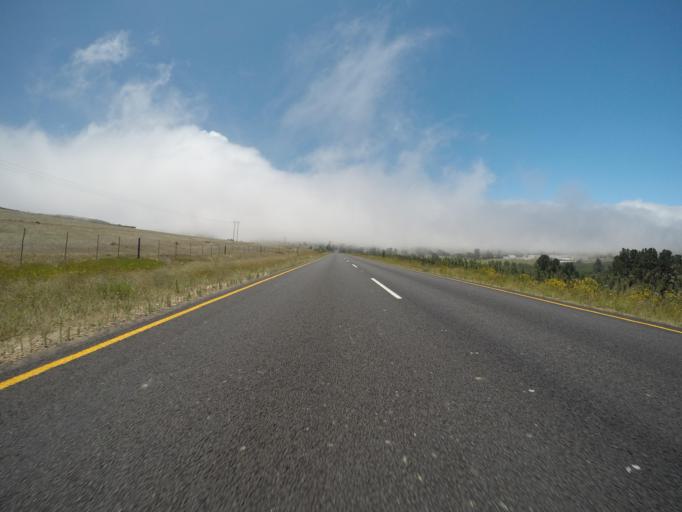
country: ZA
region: Western Cape
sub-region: Eden District Municipality
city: Knysna
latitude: -33.7267
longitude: 23.1545
